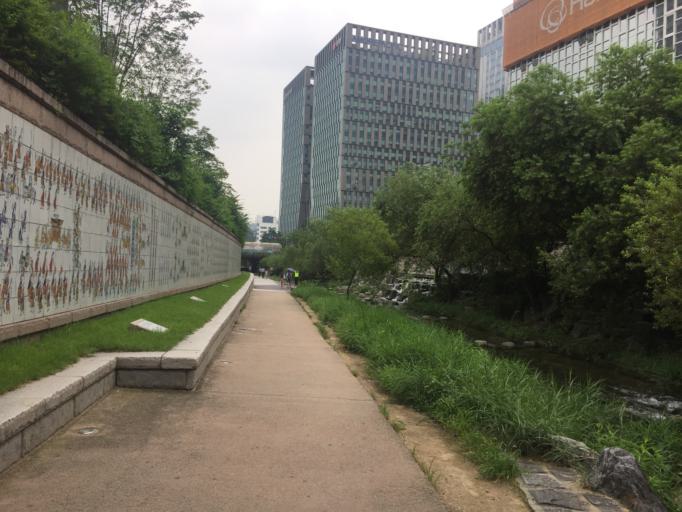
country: KR
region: Seoul
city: Seoul
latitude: 37.5683
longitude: 126.9857
